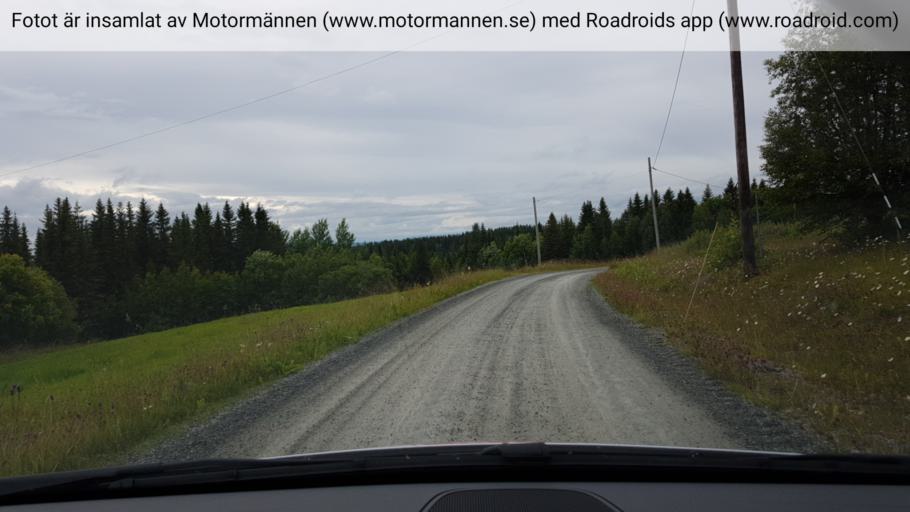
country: SE
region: Jaemtland
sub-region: Krokoms Kommun
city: Valla
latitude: 63.5722
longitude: 13.9313
